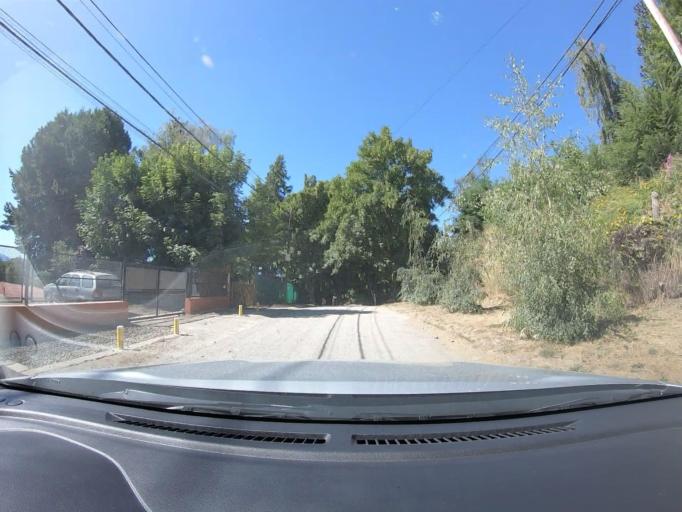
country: AR
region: Rio Negro
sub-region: Departamento de Bariloche
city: San Carlos de Bariloche
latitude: -41.1220
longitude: -71.3921
